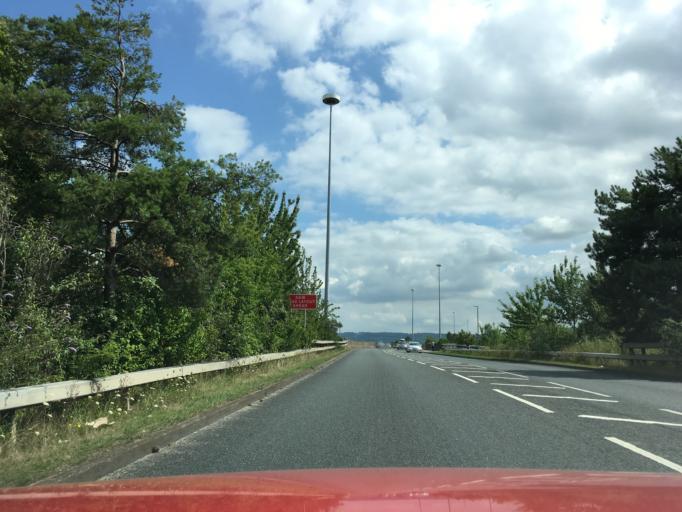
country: GB
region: England
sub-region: Gloucestershire
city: Gloucester
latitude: 51.8616
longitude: -2.2297
